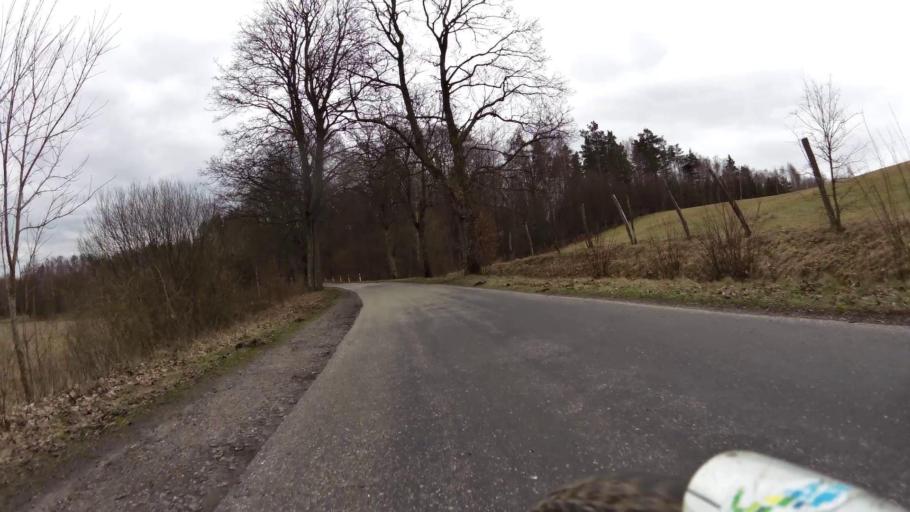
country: PL
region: Pomeranian Voivodeship
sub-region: Powiat bytowski
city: Trzebielino
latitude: 54.0987
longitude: 17.1325
